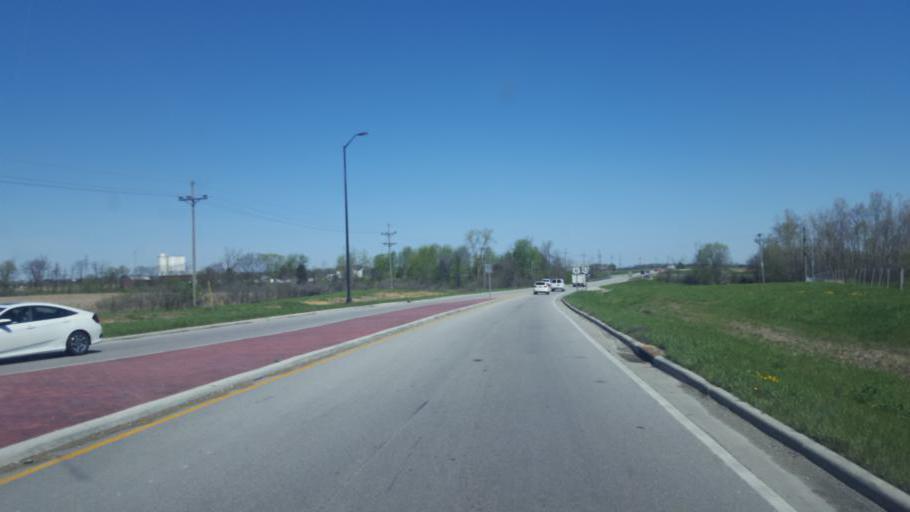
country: US
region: Ohio
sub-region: Sandusky County
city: Stony Prairie
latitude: 41.3541
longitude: -83.1651
